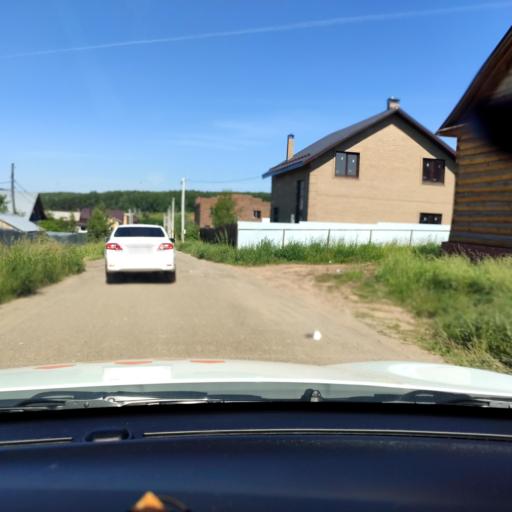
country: RU
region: Tatarstan
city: Vysokaya Gora
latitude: 55.8172
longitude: 49.2856
